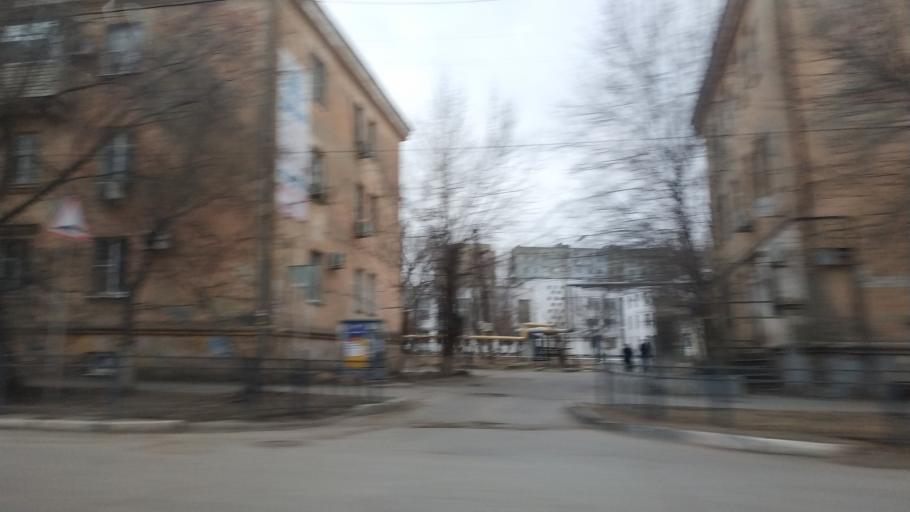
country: RU
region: Astrakhan
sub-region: Gorod Astrakhan'
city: Astrakhan'
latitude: 46.3345
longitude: 48.0158
